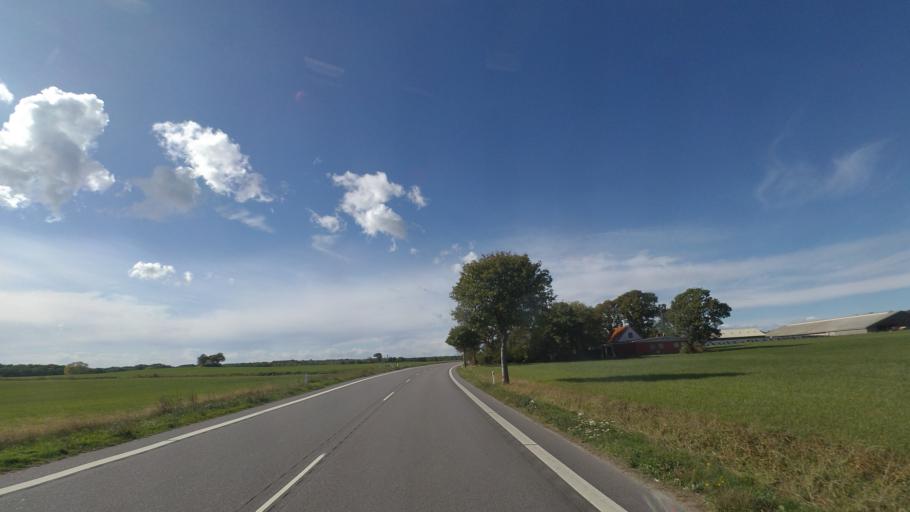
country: DK
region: Capital Region
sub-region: Bornholm Kommune
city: Ronne
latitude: 55.0747
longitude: 14.7829
